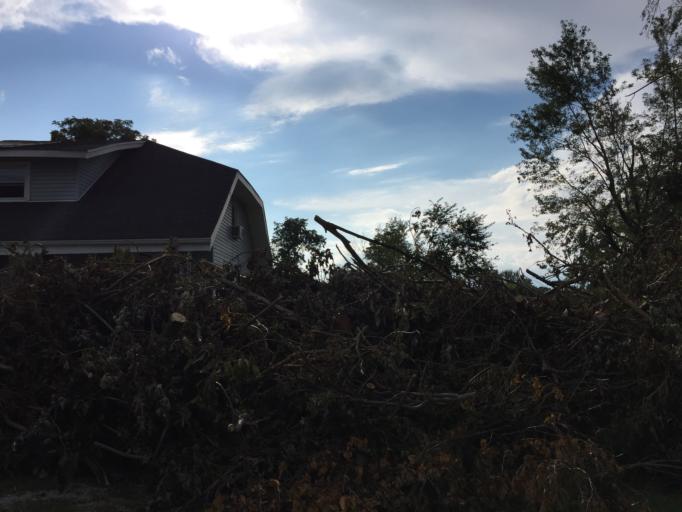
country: US
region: Indiana
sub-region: Howard County
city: Kokomo
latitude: 40.4680
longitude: -86.1138
